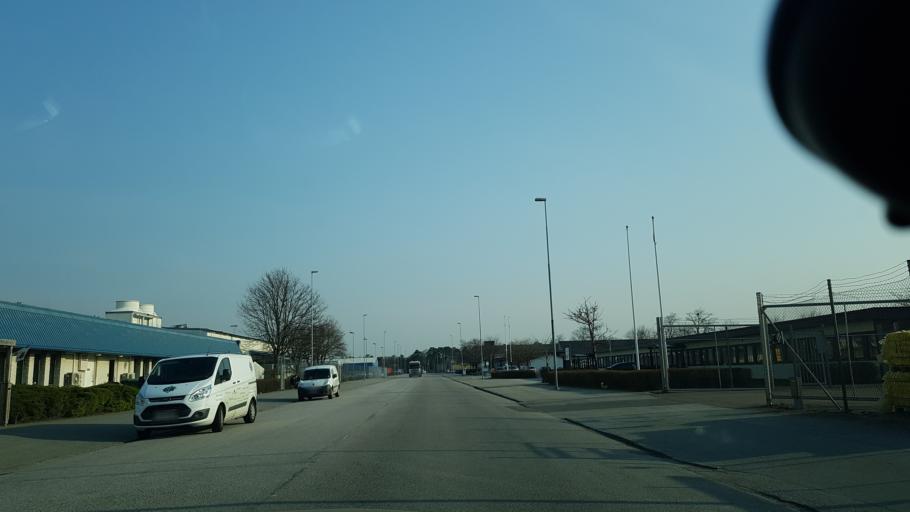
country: SE
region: Skane
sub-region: Ystads Kommun
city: Ystad
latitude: 55.4238
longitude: 13.8386
